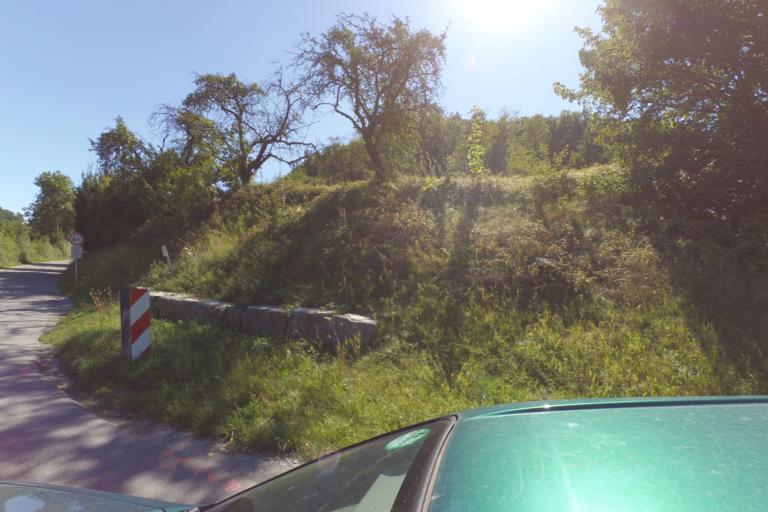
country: DE
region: Baden-Wuerttemberg
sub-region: Regierungsbezirk Stuttgart
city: Weissbach
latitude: 49.2959
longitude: 9.5916
